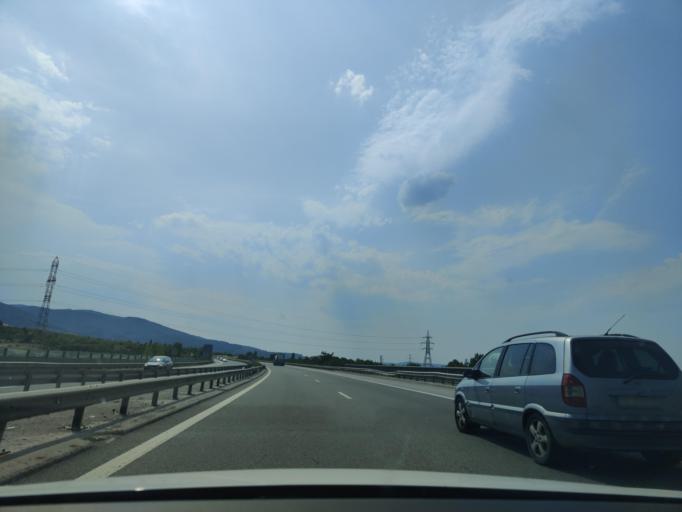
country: BG
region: Sofiya
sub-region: Obshtina Bozhurishte
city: Bozhurishte
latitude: 42.6925
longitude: 23.1680
